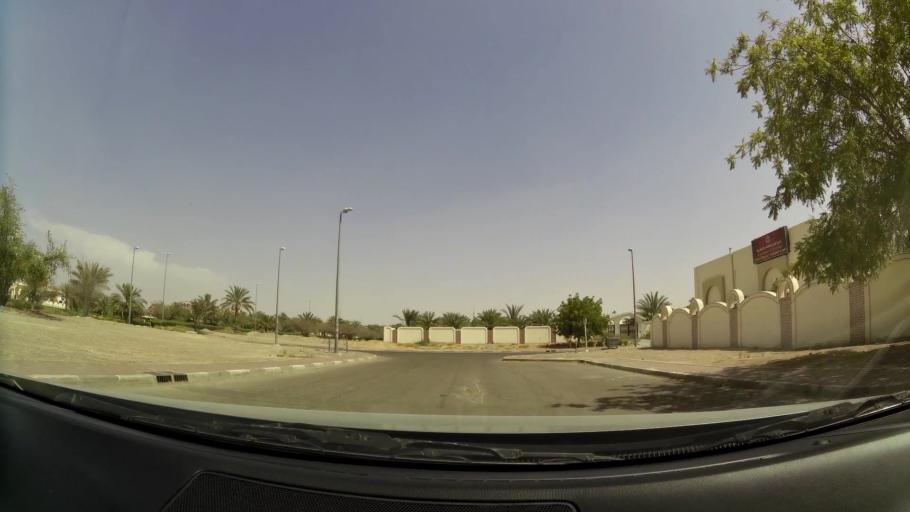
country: AE
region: Abu Dhabi
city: Al Ain
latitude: 24.2308
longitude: 55.7079
